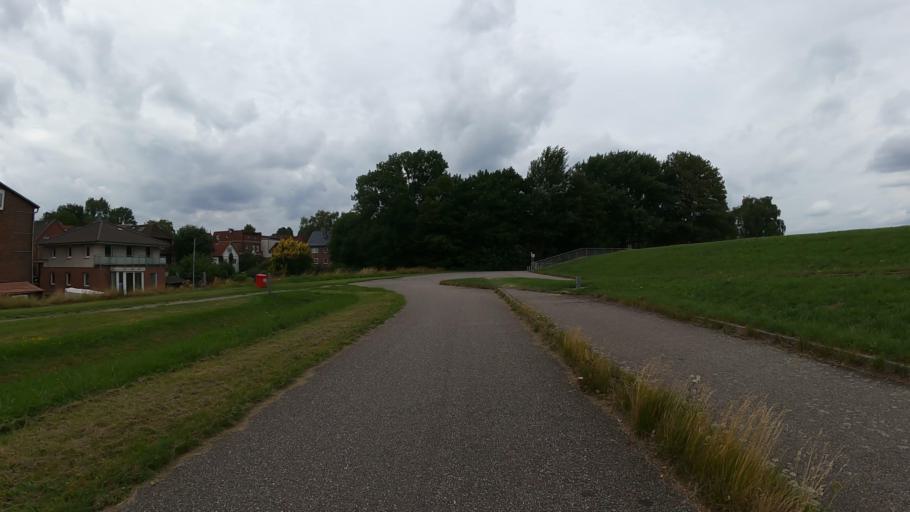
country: DE
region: Hamburg
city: Altona
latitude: 53.5277
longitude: 9.8878
